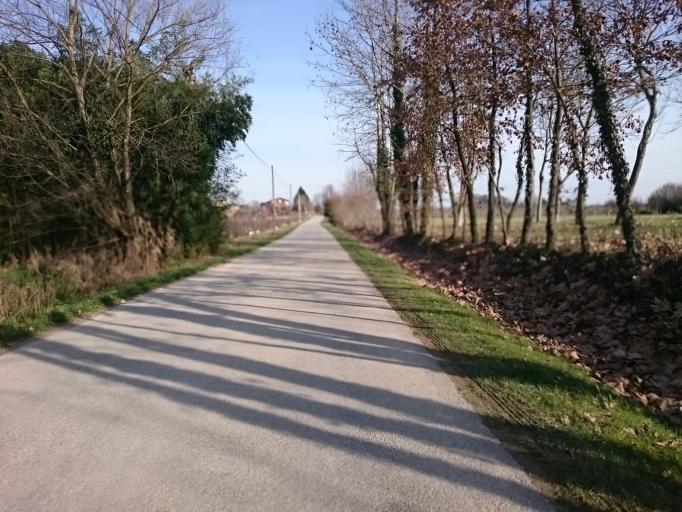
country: IT
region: Veneto
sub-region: Provincia di Verona
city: Salionze
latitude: 45.4166
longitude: 10.7057
